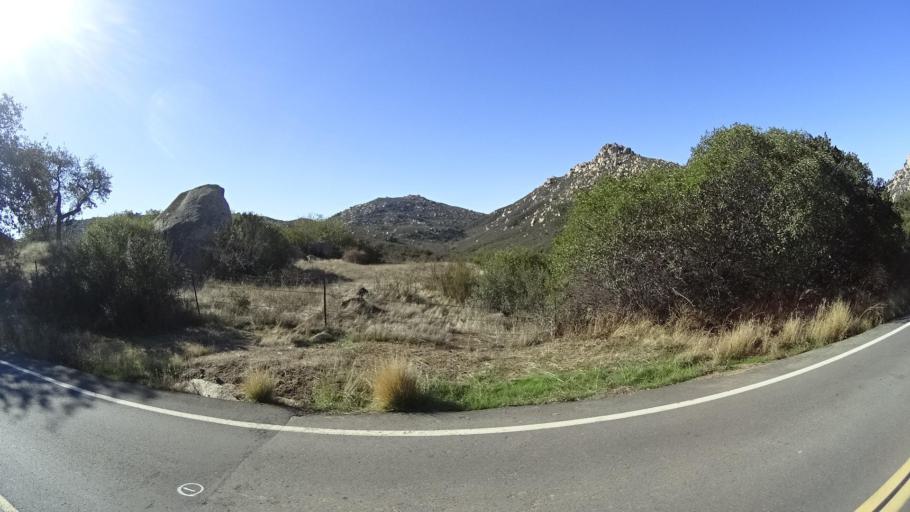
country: US
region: California
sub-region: San Diego County
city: Jamul
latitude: 32.6773
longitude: -116.7445
